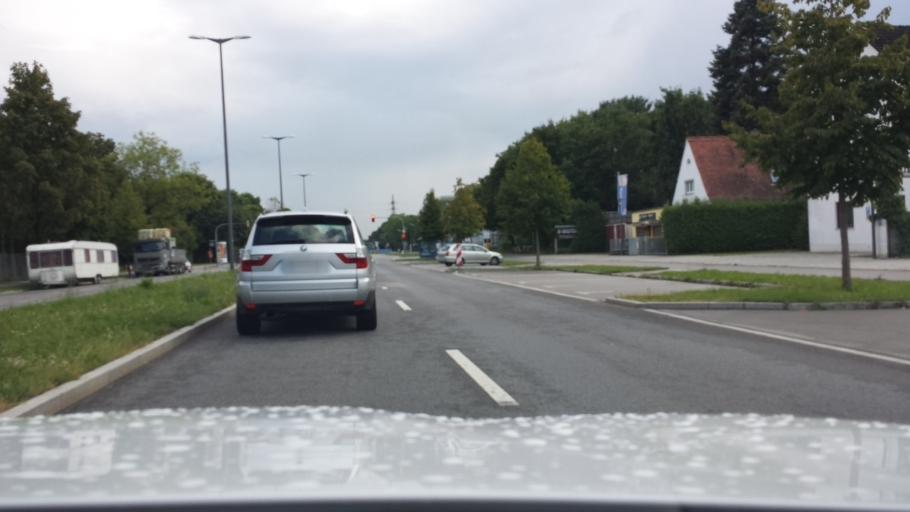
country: DE
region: Bavaria
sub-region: Upper Bavaria
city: Oberschleissheim
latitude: 48.2025
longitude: 11.5640
